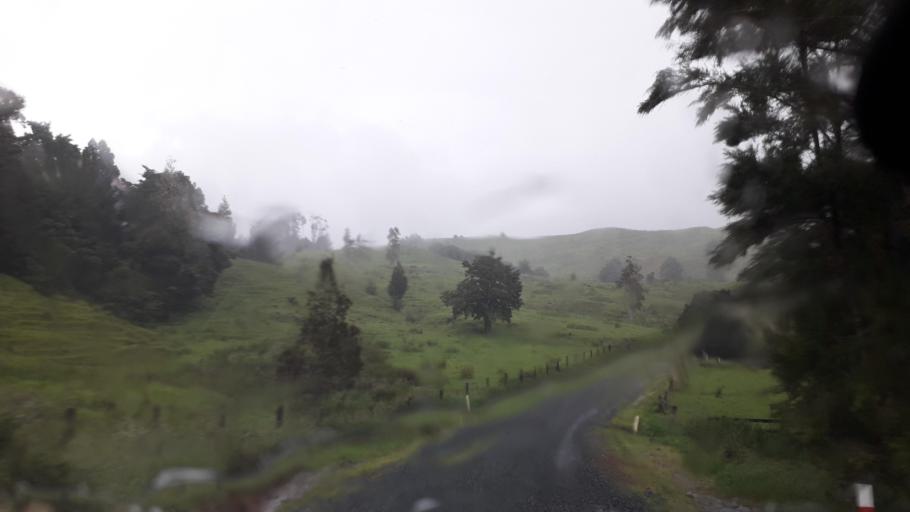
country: NZ
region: Northland
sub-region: Far North District
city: Waimate North
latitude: -35.1538
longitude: 173.7156
